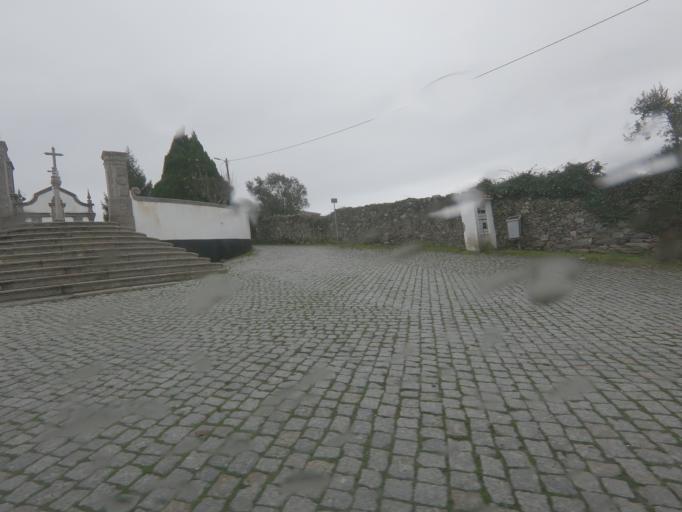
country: PT
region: Vila Real
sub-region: Peso da Regua
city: Peso da Regua
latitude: 41.1770
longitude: -7.7245
